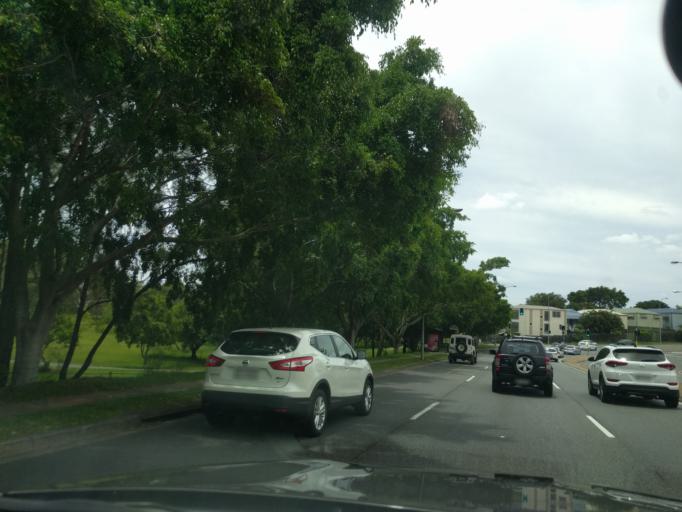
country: AU
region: Queensland
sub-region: Brisbane
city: Grange
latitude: -27.4294
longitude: 153.0046
